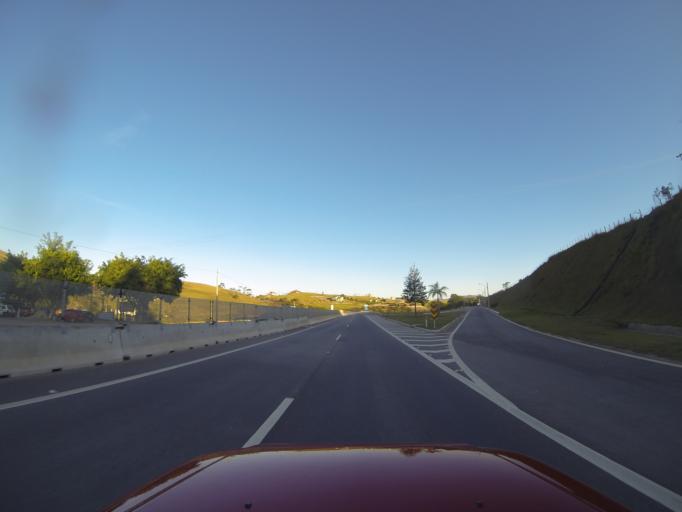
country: BR
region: Sao Paulo
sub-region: Santa Branca
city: Santa Branca
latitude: -23.4362
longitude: -45.6198
